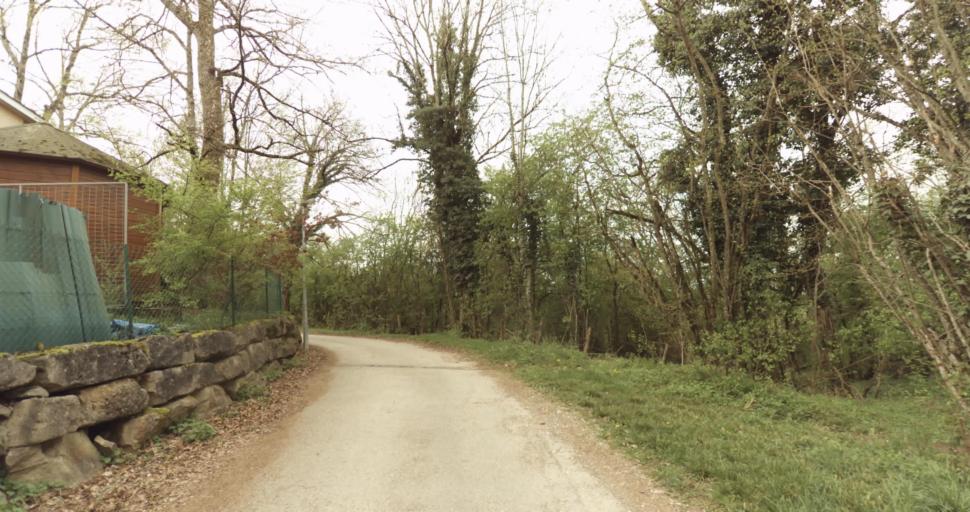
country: FR
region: Rhone-Alpes
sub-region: Departement de l'Ain
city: Amberieu-en-Bugey
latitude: 45.9655
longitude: 5.3703
